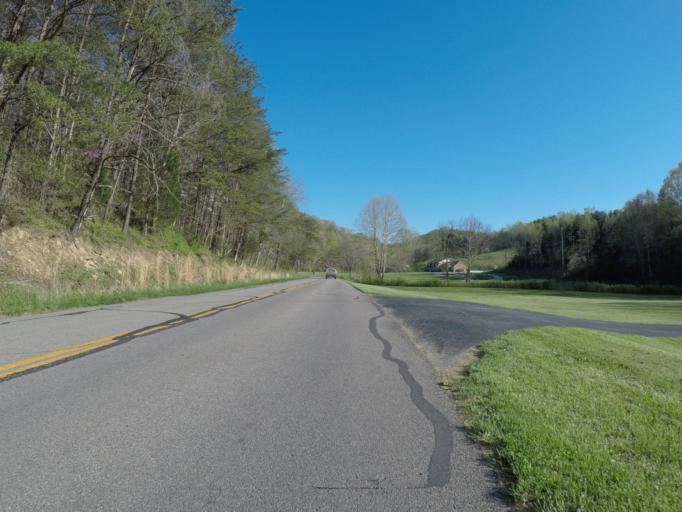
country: US
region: Kentucky
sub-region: Boyd County
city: Meads
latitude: 38.3649
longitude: -82.6783
